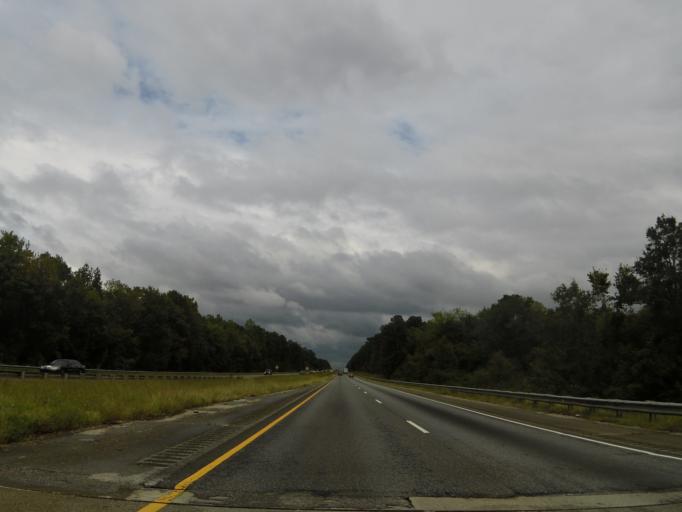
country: US
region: Alabama
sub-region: Escambia County
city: Brewton
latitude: 31.3071
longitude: -87.1631
